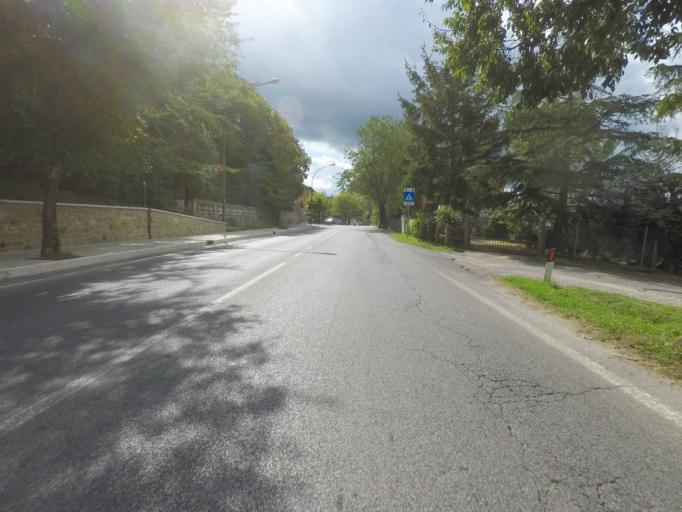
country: IT
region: Tuscany
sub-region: Provincia di Siena
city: Montepulciano
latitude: 43.1057
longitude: 11.7860
